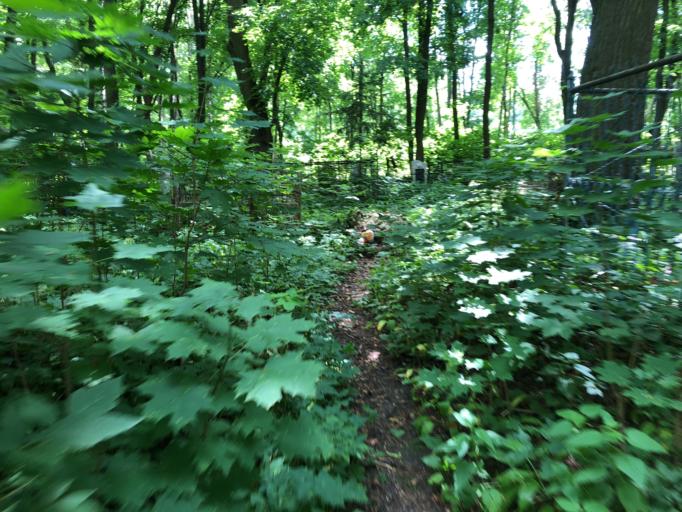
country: RU
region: Tula
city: Tula
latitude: 54.1785
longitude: 37.6077
